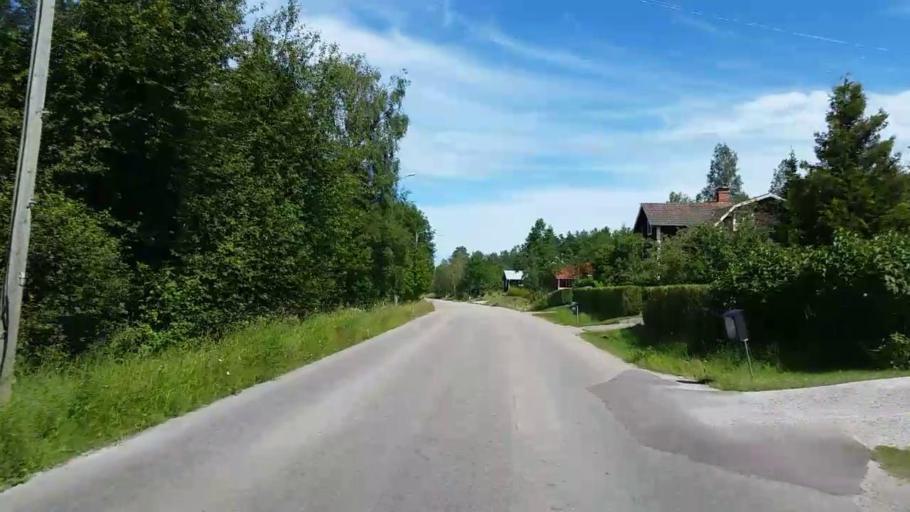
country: SE
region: Dalarna
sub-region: Rattviks Kommun
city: Raettvik
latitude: 60.8864
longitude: 15.1357
